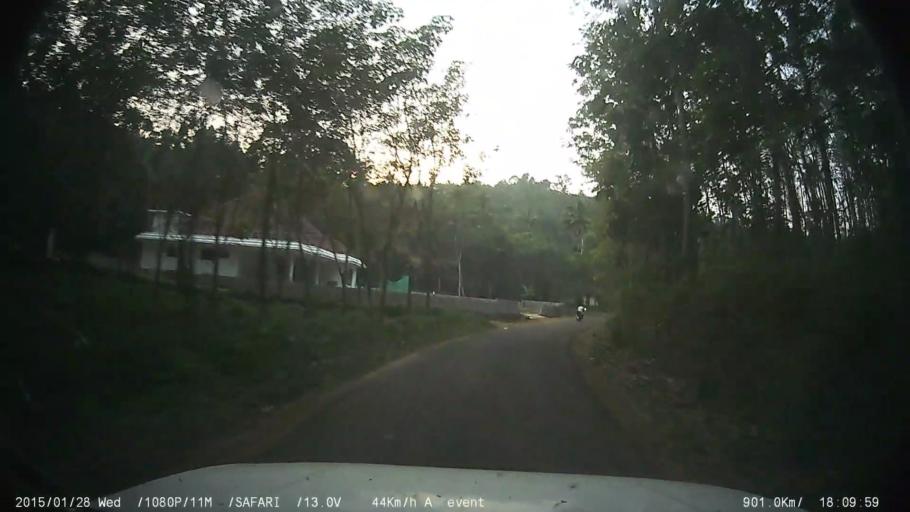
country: IN
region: Kerala
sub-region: Kottayam
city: Palackattumala
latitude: 9.7442
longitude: 76.5712
